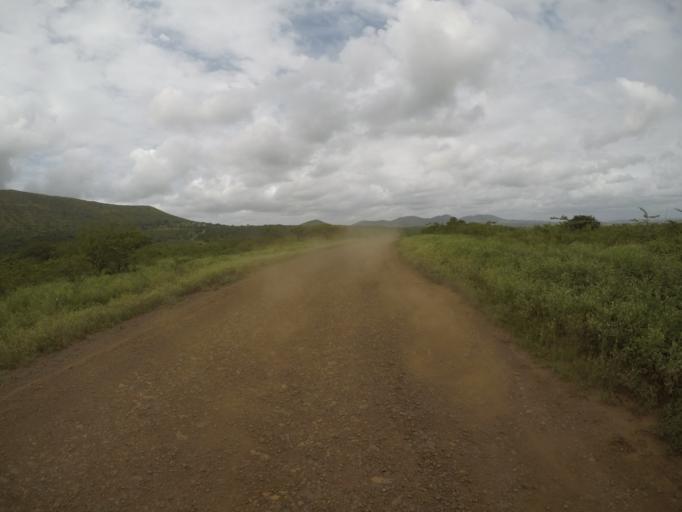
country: ZA
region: KwaZulu-Natal
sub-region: uThungulu District Municipality
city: Empangeni
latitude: -28.5932
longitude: 31.8909
